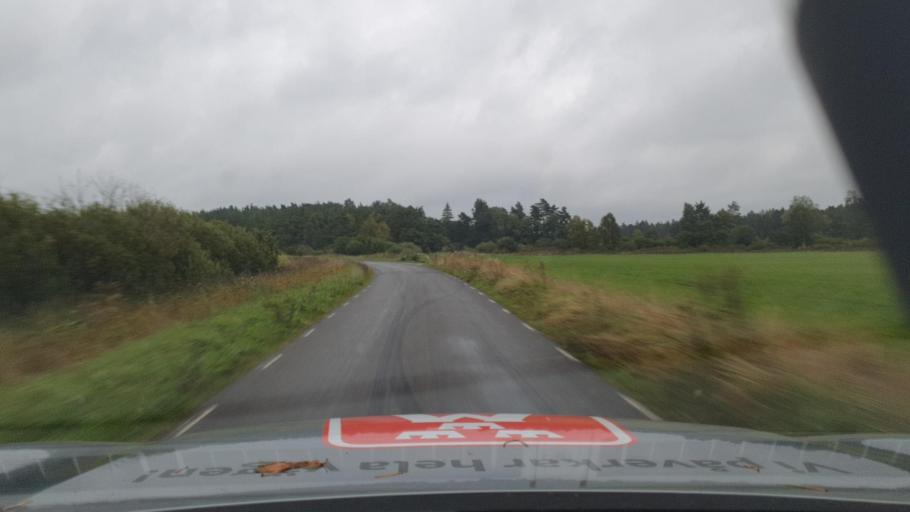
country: SE
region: Gotland
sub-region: Gotland
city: Hemse
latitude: 57.4289
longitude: 18.4005
